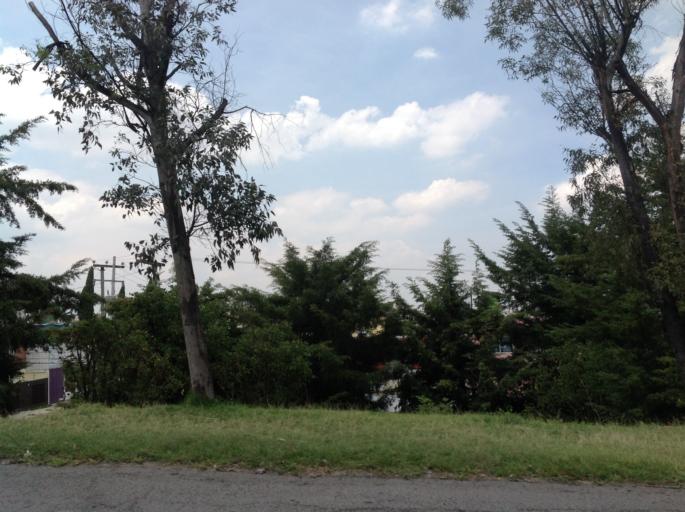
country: MX
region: Mexico
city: Ciudad Lopez Mateos
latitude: 19.5950
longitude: -99.2292
